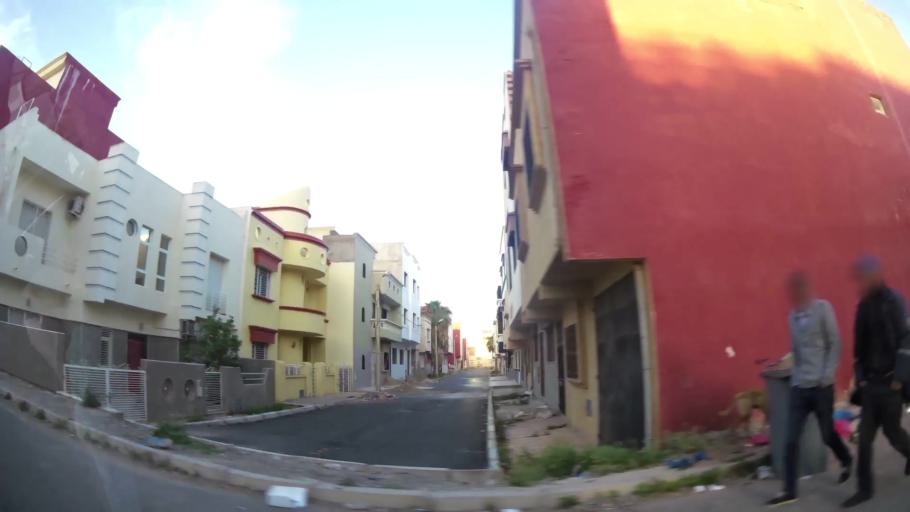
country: MA
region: Oriental
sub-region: Berkane-Taourirt
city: Madagh
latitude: 35.0797
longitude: -2.2371
